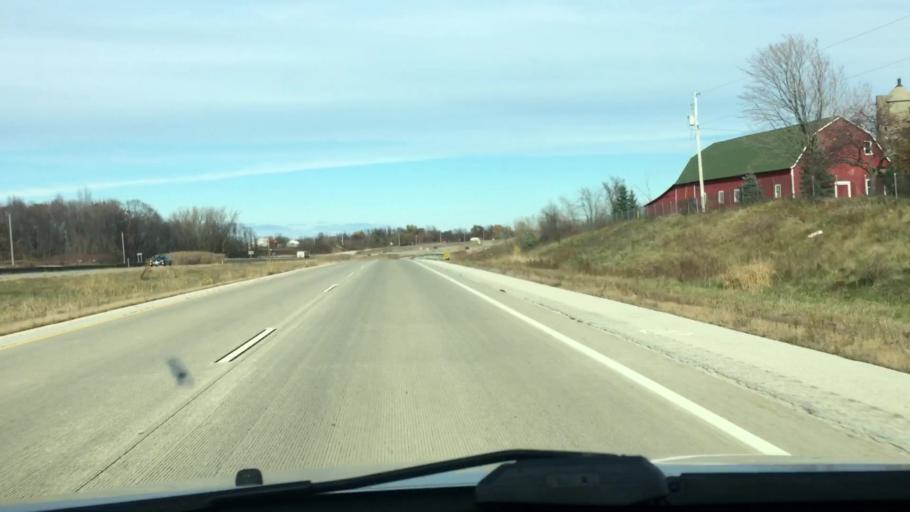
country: US
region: Wisconsin
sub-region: Kewaunee County
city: Luxemburg
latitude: 44.6645
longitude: -87.7437
